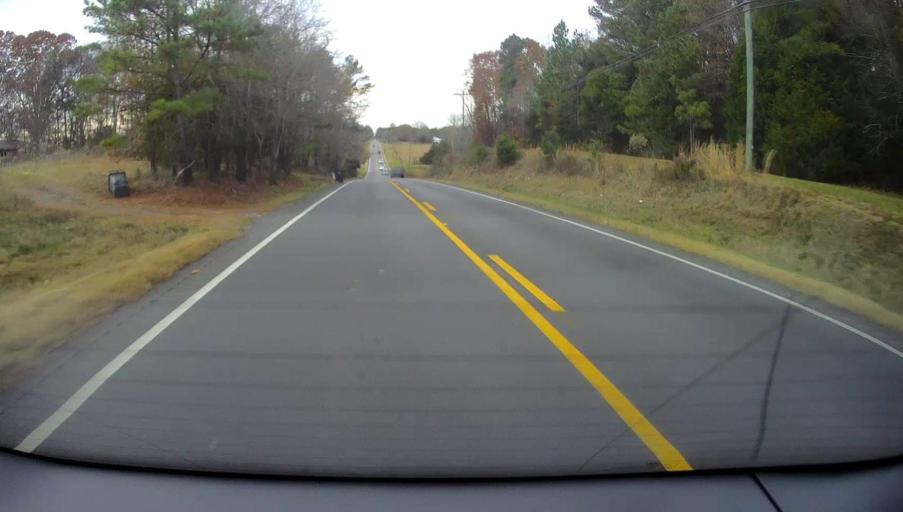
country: US
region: Alabama
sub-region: Morgan County
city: Priceville
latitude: 34.4520
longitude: -86.7656
